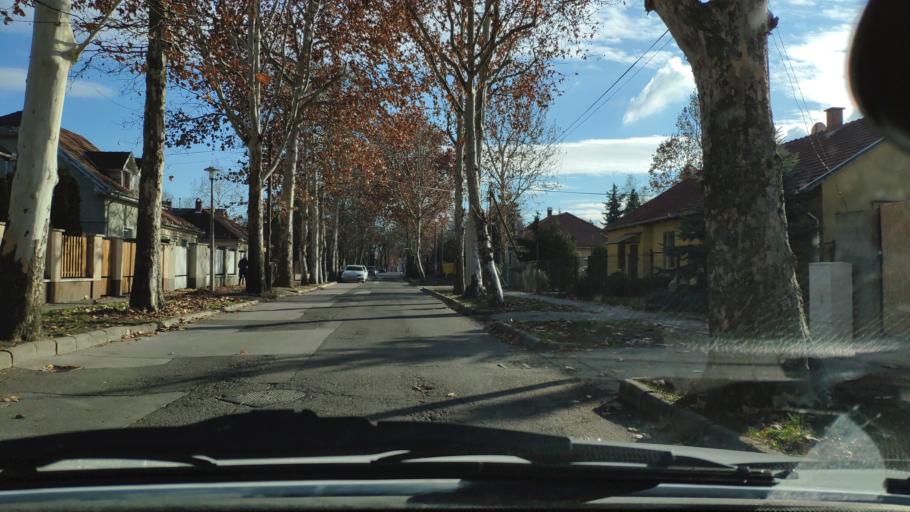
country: HU
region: Budapest
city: Budapest XXI. keruelet
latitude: 47.4119
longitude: 19.0636
